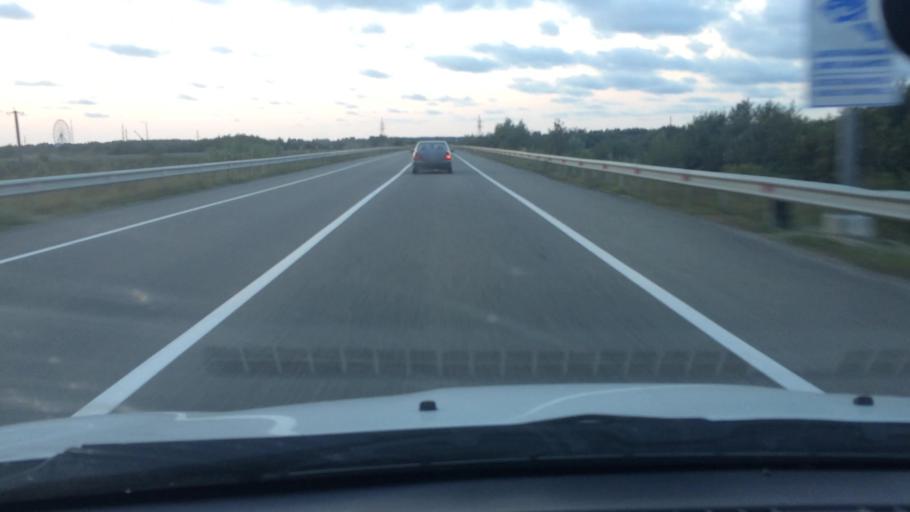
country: GE
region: Ajaria
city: Ochkhamuri
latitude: 41.9008
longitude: 41.7945
